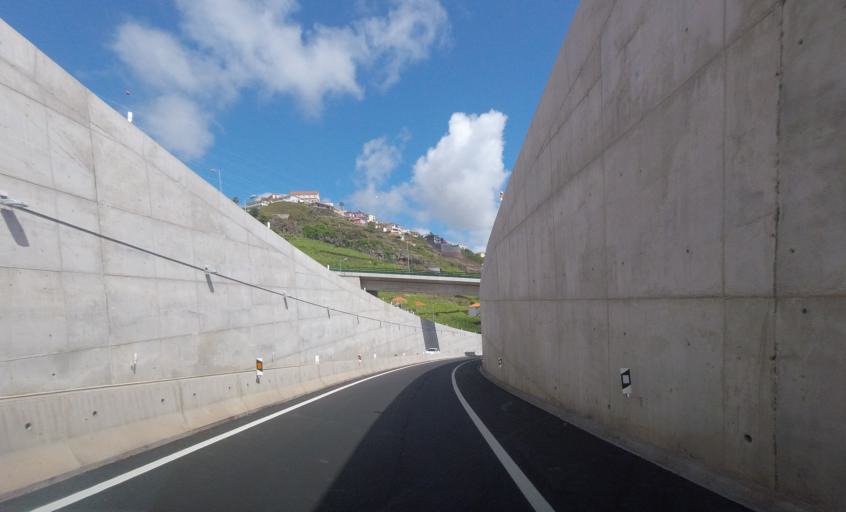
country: PT
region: Madeira
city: Camara de Lobos
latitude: 32.6698
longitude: -16.9719
